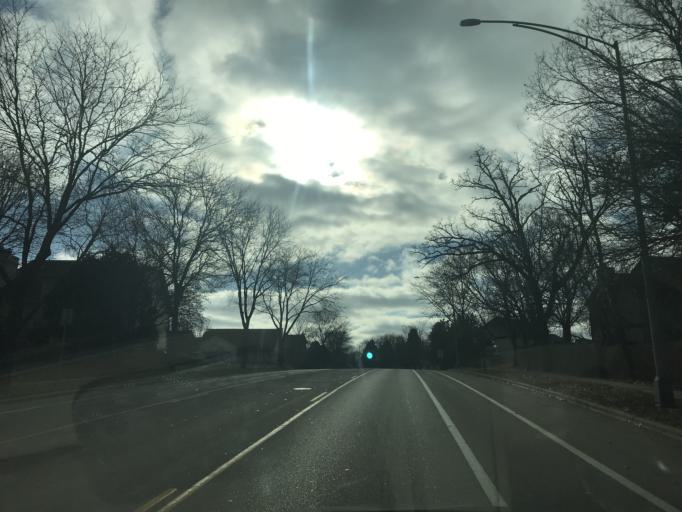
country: US
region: Wisconsin
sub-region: Dane County
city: Monona
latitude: 43.1189
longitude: -89.2977
